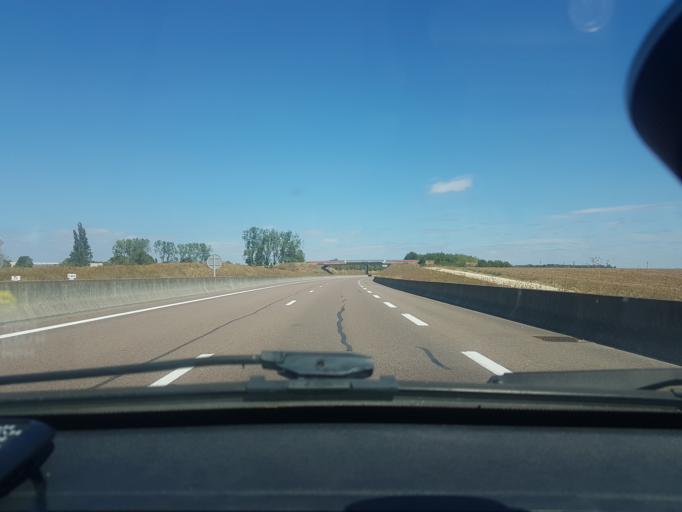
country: FR
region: Bourgogne
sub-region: Departement de la Cote-d'Or
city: Quetigny
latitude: 47.3312
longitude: 5.1066
